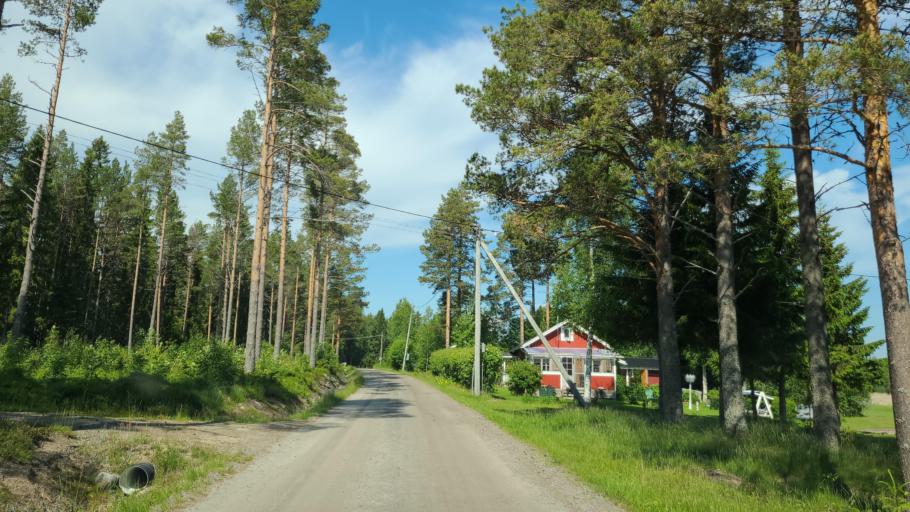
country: SE
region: Vaesterbotten
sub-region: Robertsfors Kommun
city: Robertsfors
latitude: 64.1432
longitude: 20.9628
